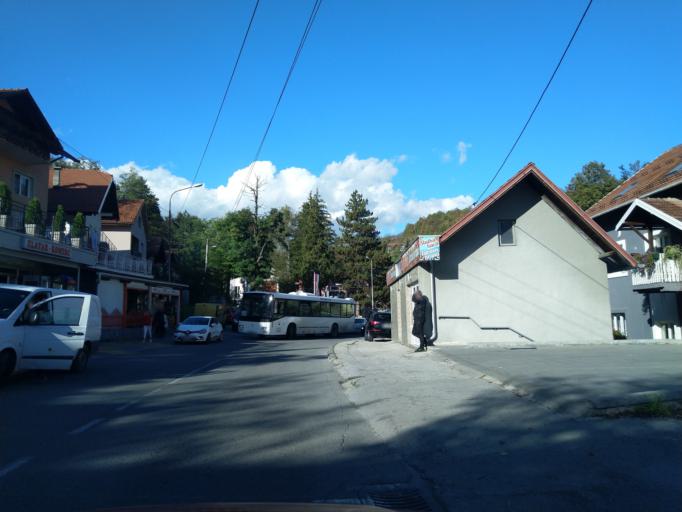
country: RS
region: Central Serbia
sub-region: Zlatiborski Okrug
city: Uzice
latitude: 43.8630
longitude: 19.8245
